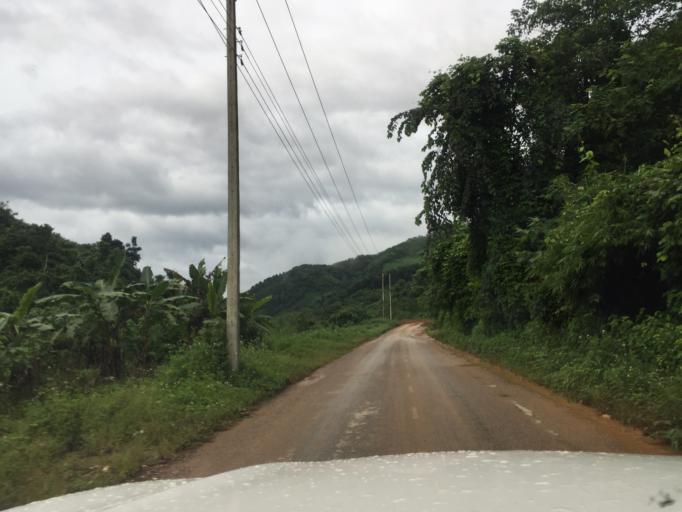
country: LA
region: Oudomxai
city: Muang La
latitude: 21.0235
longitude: 102.2337
